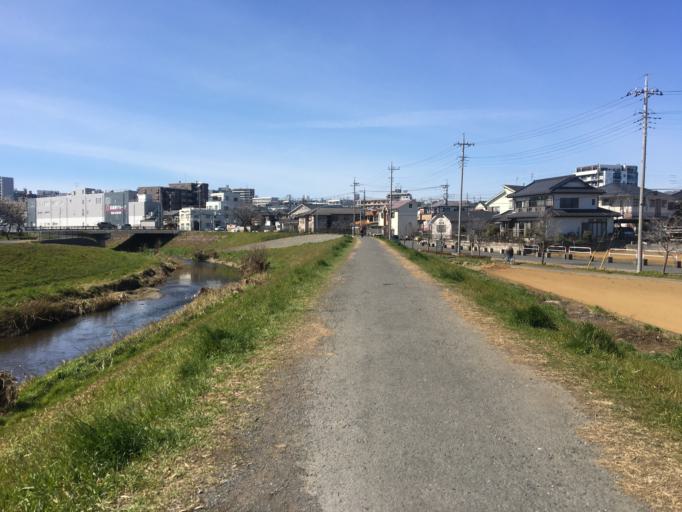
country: JP
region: Saitama
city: Asaka
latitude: 35.8169
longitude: 139.5965
